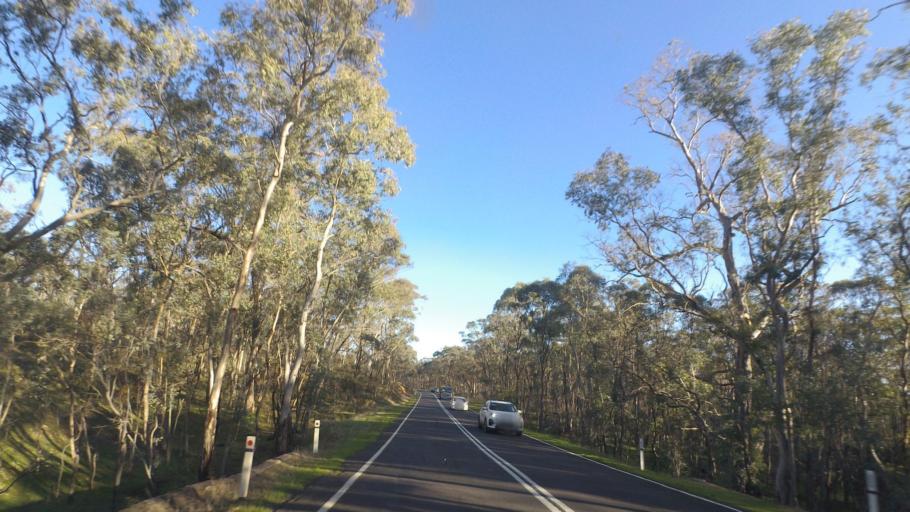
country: AU
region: Victoria
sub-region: Greater Bendigo
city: Kennington
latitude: -36.9165
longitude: 144.4921
